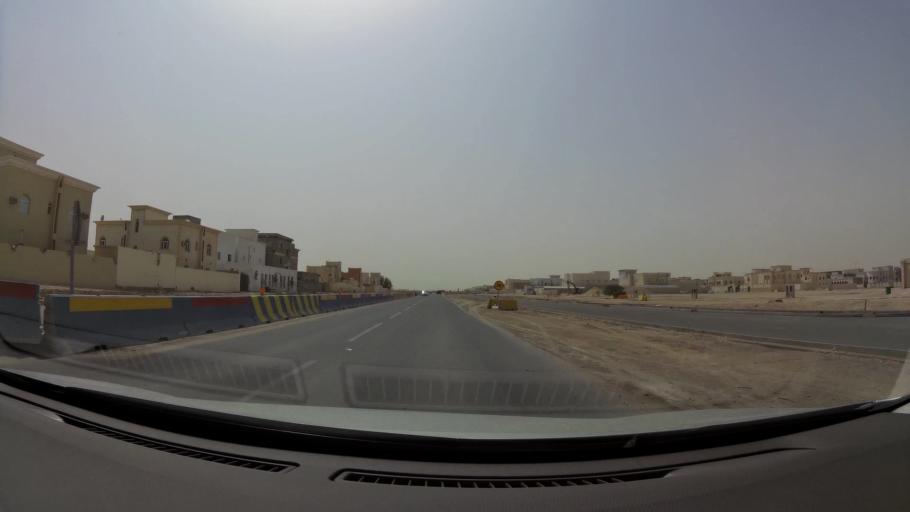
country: QA
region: Baladiyat ar Rayyan
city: Ar Rayyan
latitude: 25.2521
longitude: 51.3638
